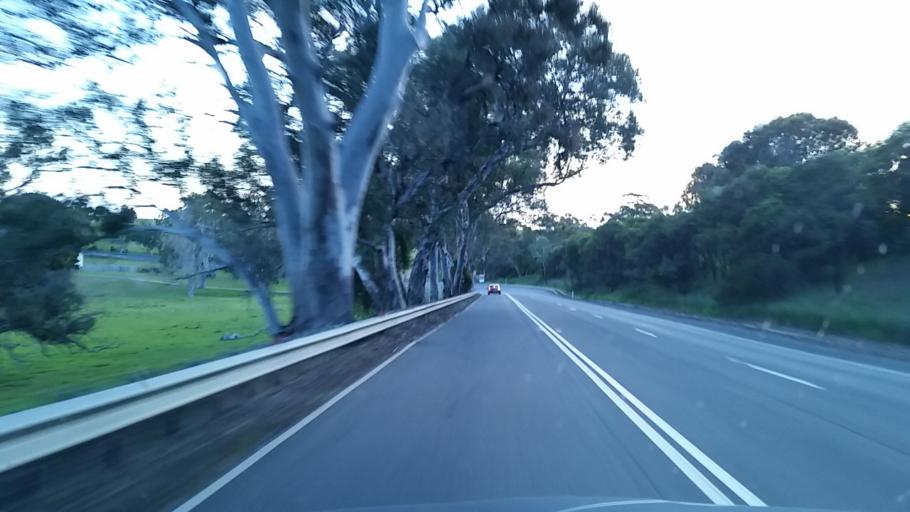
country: AU
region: South Australia
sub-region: Yankalilla
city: Normanville
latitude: -35.4490
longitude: 138.3633
